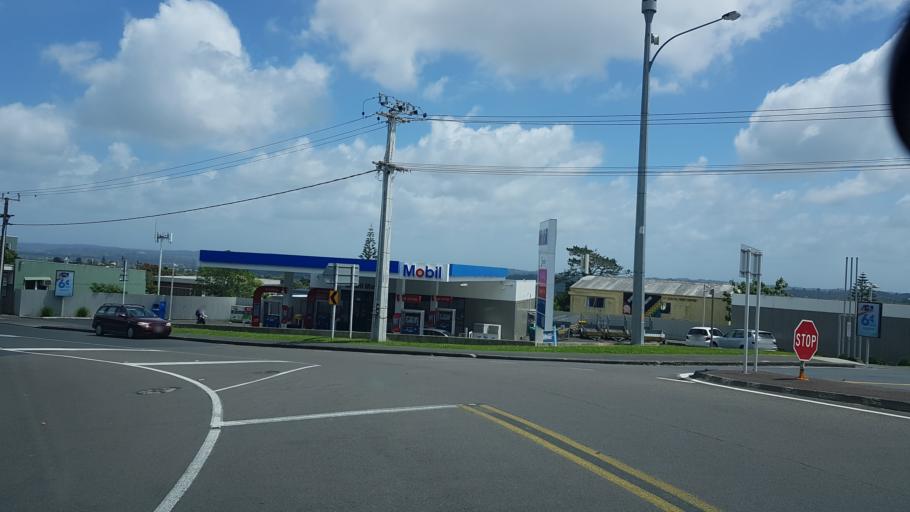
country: NZ
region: Auckland
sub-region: Auckland
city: North Shore
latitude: -36.8065
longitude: 174.7065
